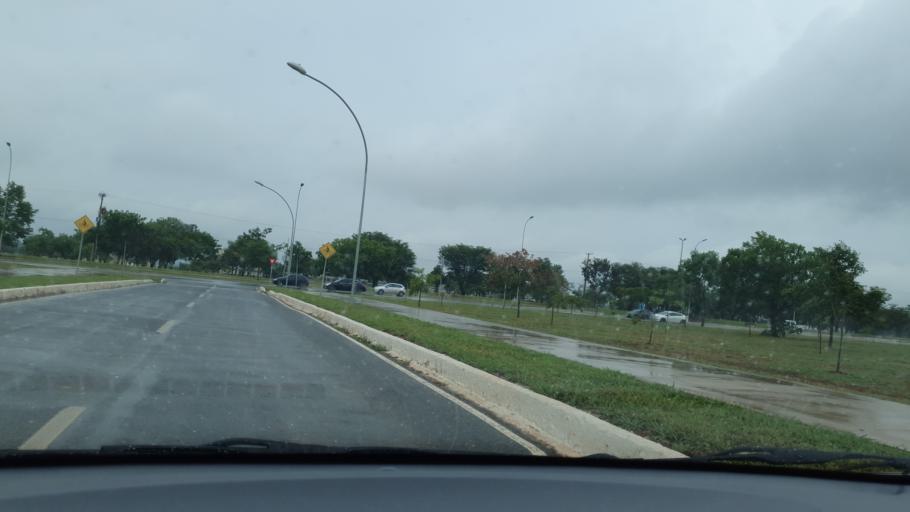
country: BR
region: Federal District
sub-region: Brasilia
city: Brasilia
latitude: -15.7817
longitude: -47.9209
